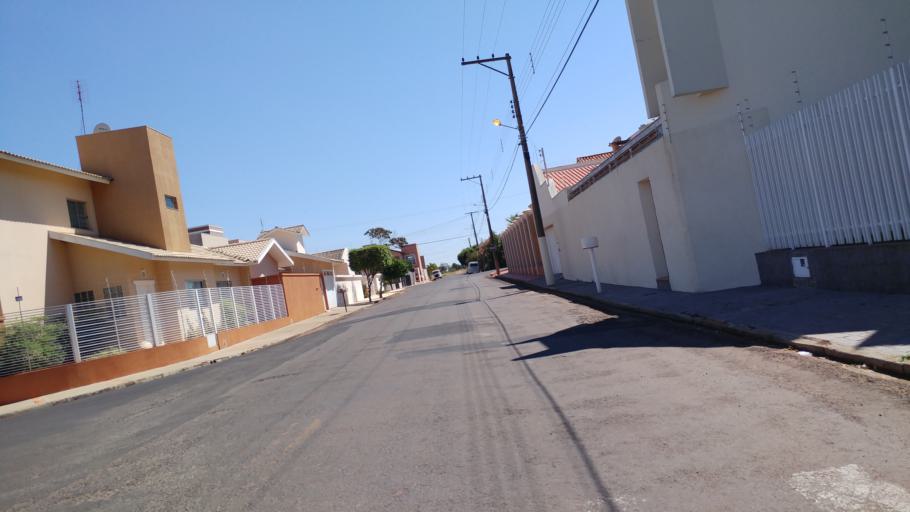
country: BR
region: Sao Paulo
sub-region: Paraguacu Paulista
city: Paraguacu Paulista
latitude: -22.4115
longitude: -50.5857
